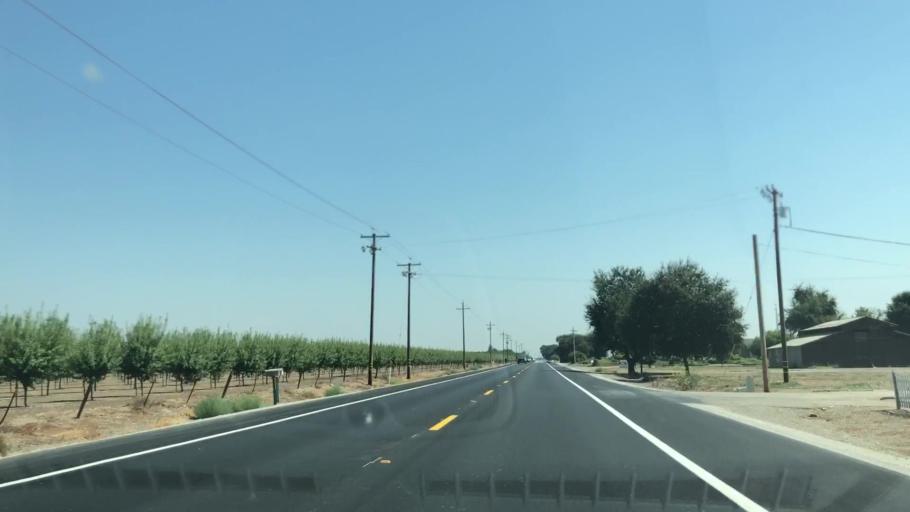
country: US
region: California
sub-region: San Joaquin County
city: Garden Acres
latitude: 37.9422
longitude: -121.1378
